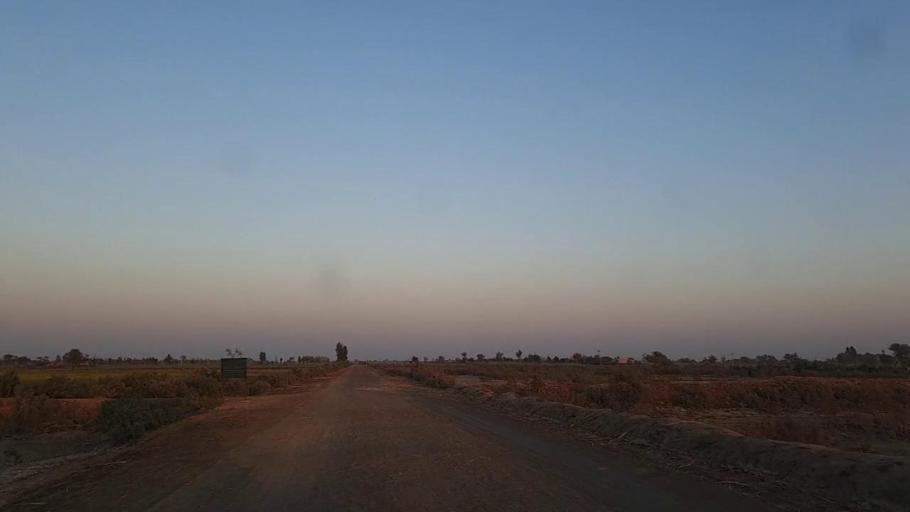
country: PK
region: Sindh
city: Samaro
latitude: 25.3093
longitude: 69.3768
